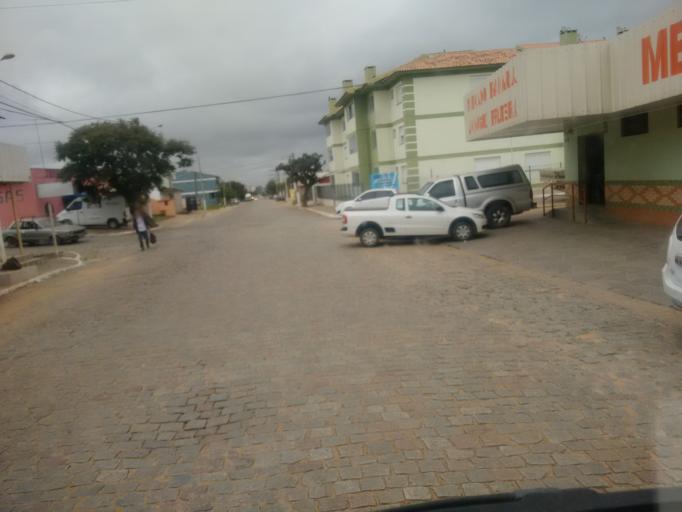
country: BR
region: Rio Grande do Sul
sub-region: Camaqua
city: Camaqua
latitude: -30.8386
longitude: -51.8153
